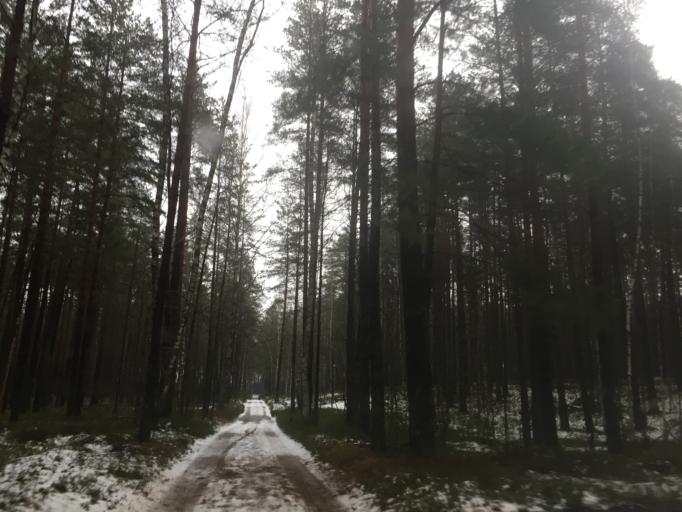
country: LV
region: Stopini
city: Ulbroka
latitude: 56.9547
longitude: 24.3319
